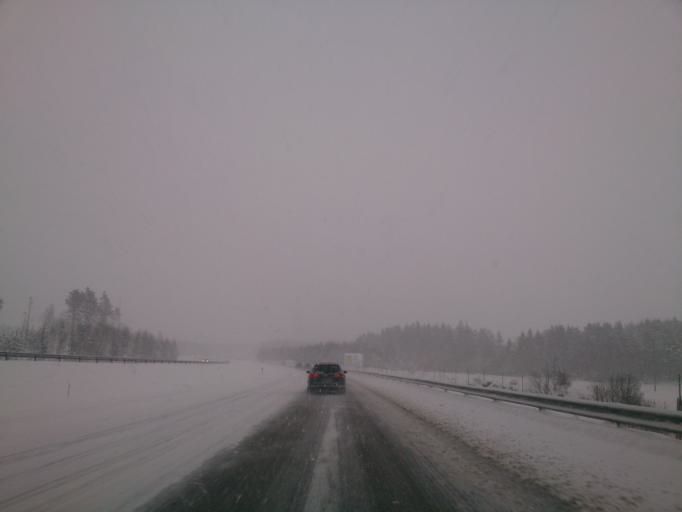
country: SE
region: Soedermanland
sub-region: Nykopings Kommun
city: Svalsta
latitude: 58.7504
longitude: 16.8861
